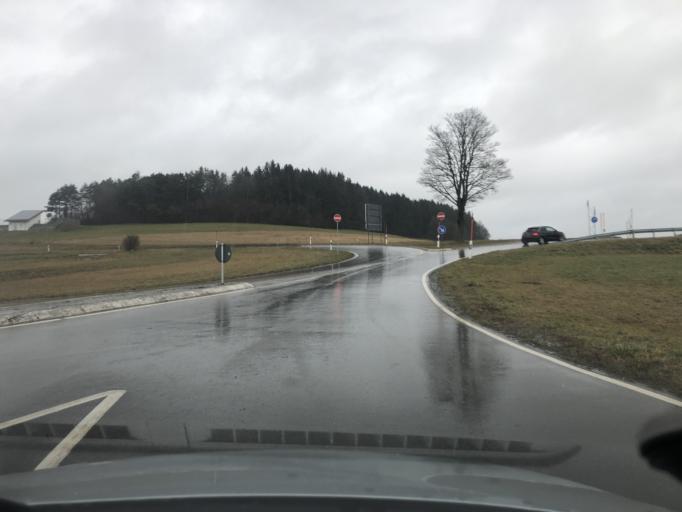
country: DE
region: Baden-Wuerttemberg
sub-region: Freiburg Region
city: Dogern
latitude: 47.6621
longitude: 8.1633
